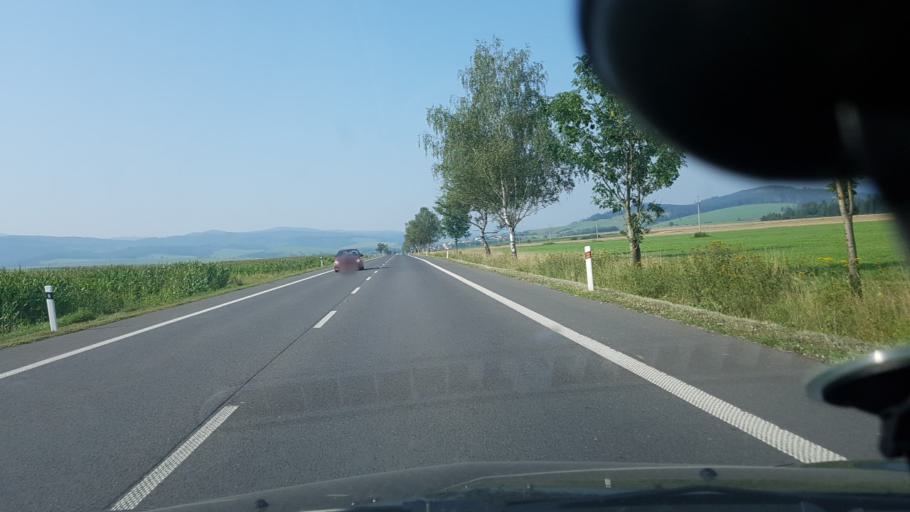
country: SK
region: Zilinsky
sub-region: Okres Zilina
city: Trstena
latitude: 49.3890
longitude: 19.6401
